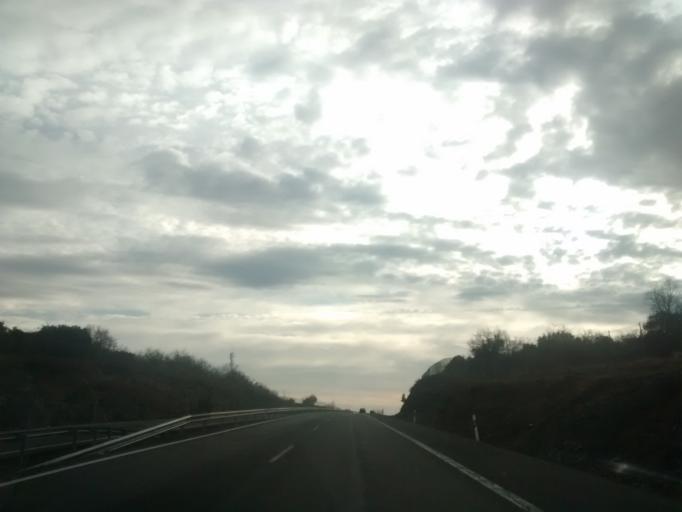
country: ES
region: Basque Country
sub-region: Provincia de Alava
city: Murguia
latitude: 42.9301
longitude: -2.7397
